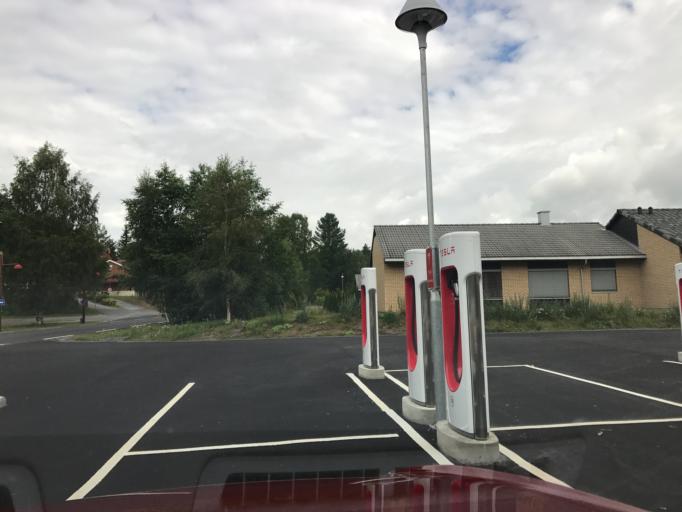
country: NO
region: Buskerud
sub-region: Flesberg
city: Lampeland
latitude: 59.8361
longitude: 9.5793
